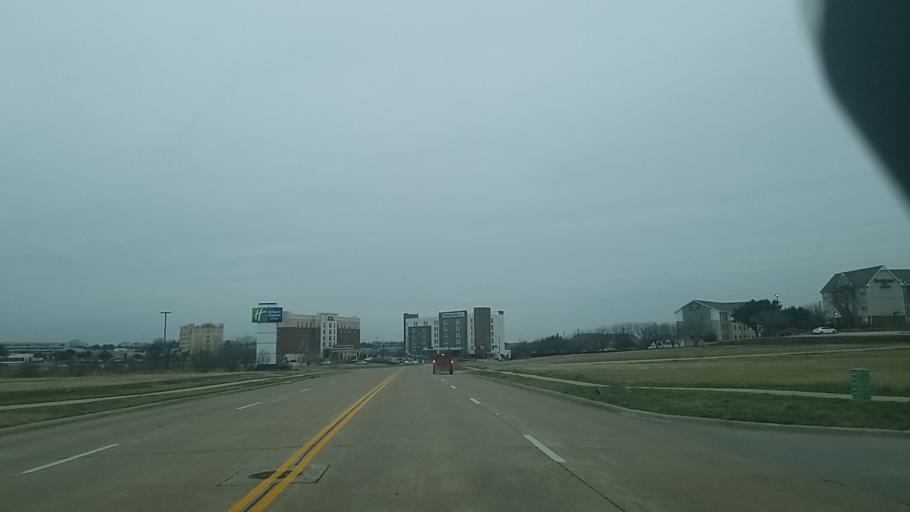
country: US
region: Texas
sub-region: Denton County
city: Lewisville
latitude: 33.0008
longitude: -96.9662
